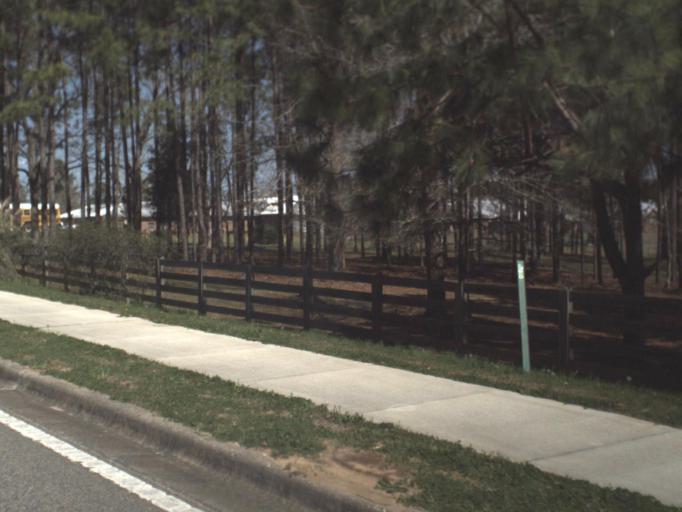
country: US
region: Florida
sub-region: Gadsden County
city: Quincy
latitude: 30.5513
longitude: -84.5922
